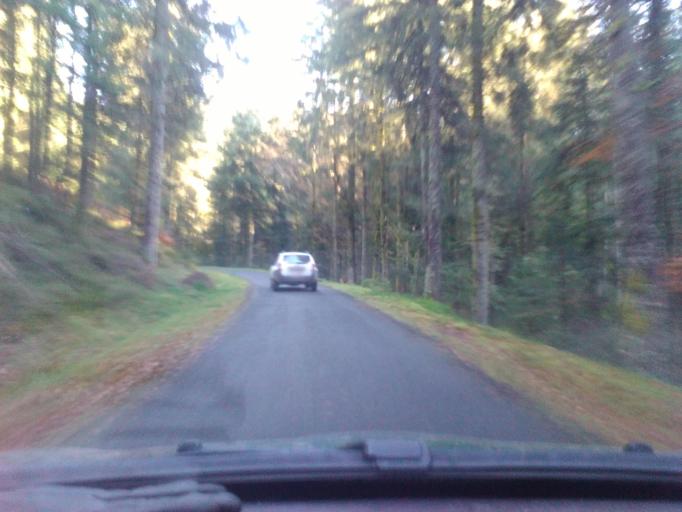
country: FR
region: Lorraine
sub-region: Departement des Vosges
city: Senones
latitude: 48.4698
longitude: 7.0790
